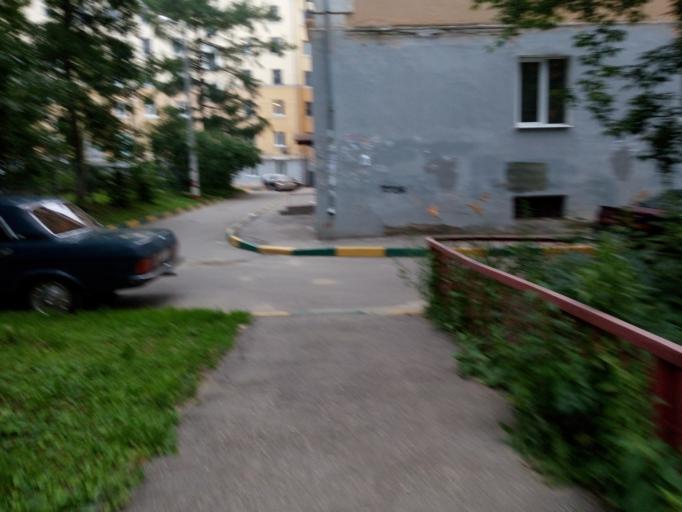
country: RU
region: Nizjnij Novgorod
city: Nizhniy Novgorod
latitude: 56.2736
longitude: 43.9793
